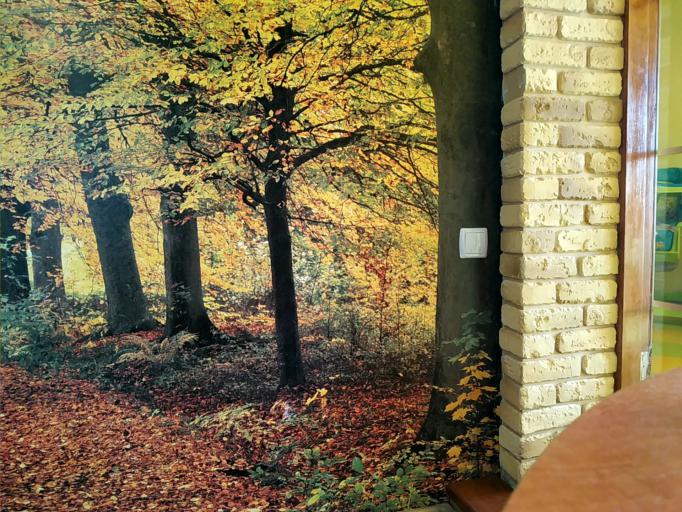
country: RU
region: Novgorod
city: Staraya Russa
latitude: 57.8331
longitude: 31.4826
